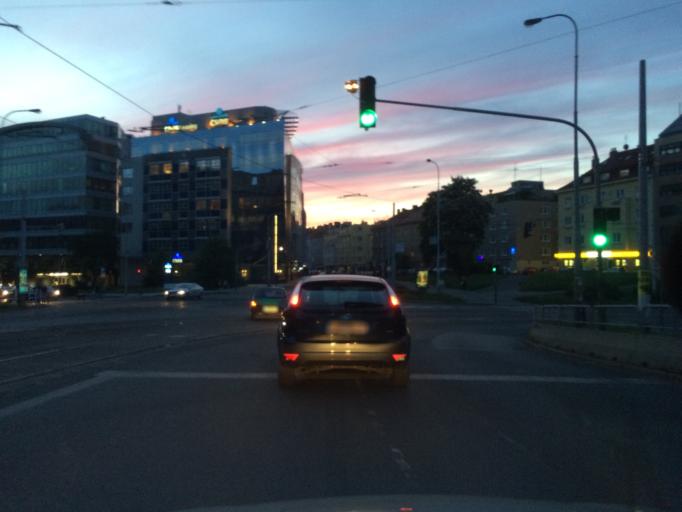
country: CZ
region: Praha
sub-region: Praha 2
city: Vysehrad
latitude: 50.0564
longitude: 14.4347
